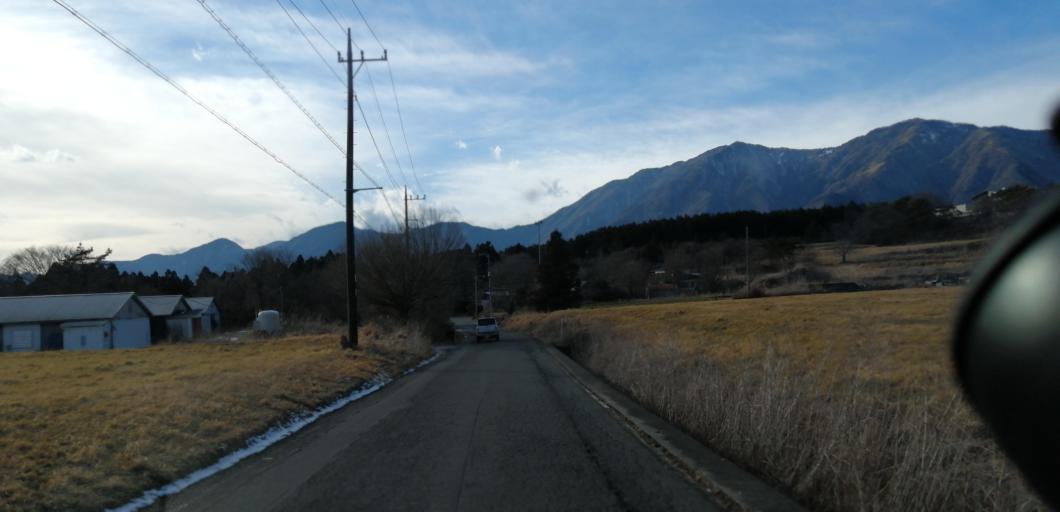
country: JP
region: Yamanashi
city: Fujikawaguchiko
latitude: 35.4023
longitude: 138.6096
